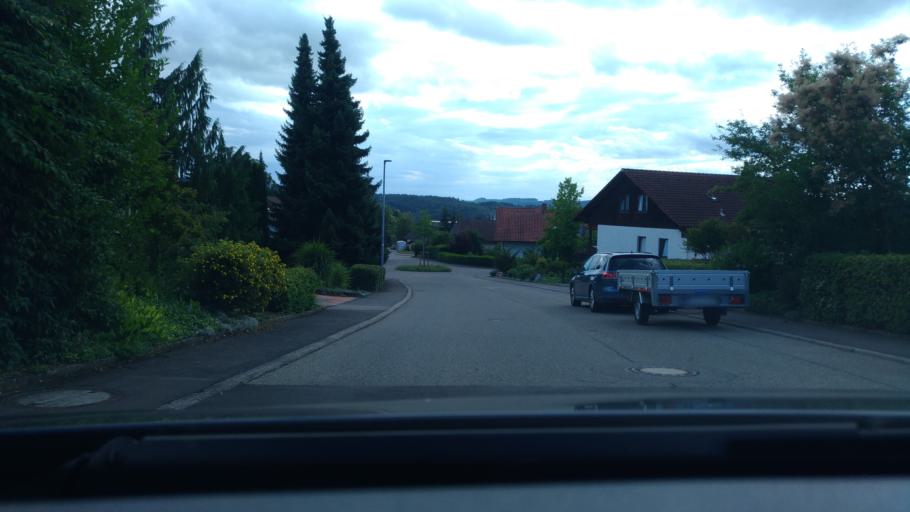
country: DE
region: Baden-Wuerttemberg
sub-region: Freiburg Region
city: Stockach
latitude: 47.8590
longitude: 9.0144
